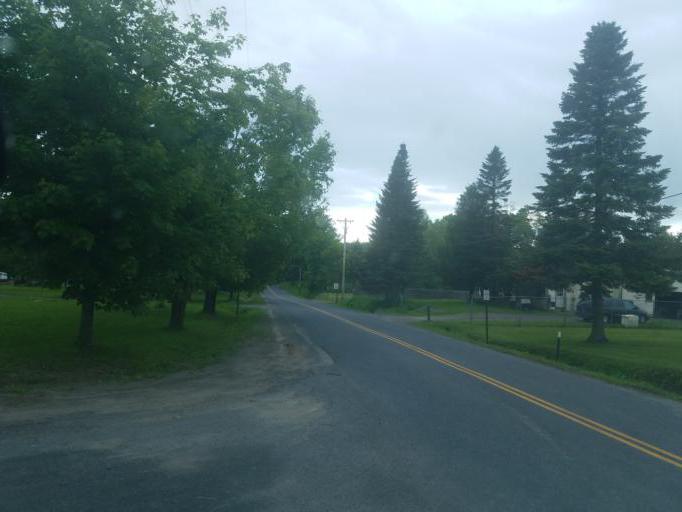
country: US
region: New York
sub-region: Herkimer County
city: Herkimer
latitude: 43.2088
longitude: -74.9527
